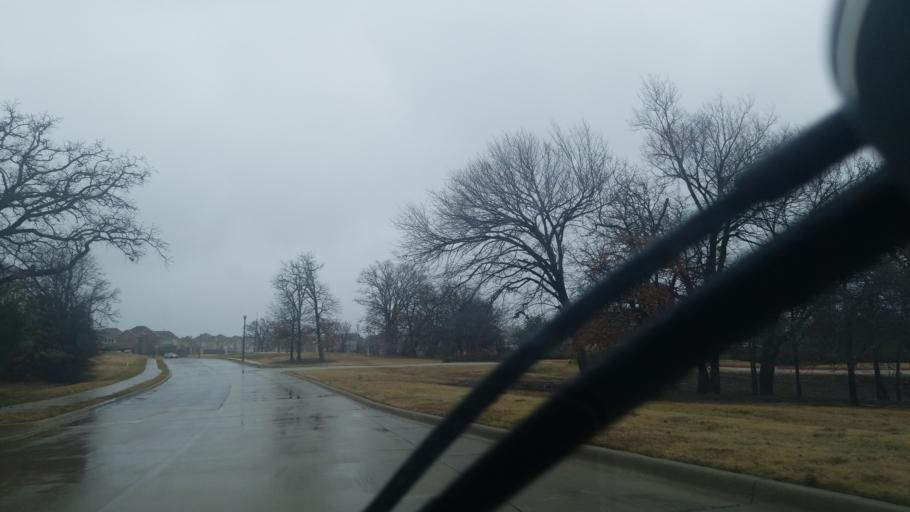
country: US
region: Texas
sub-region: Denton County
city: Corinth
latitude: 33.1759
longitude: -97.0590
